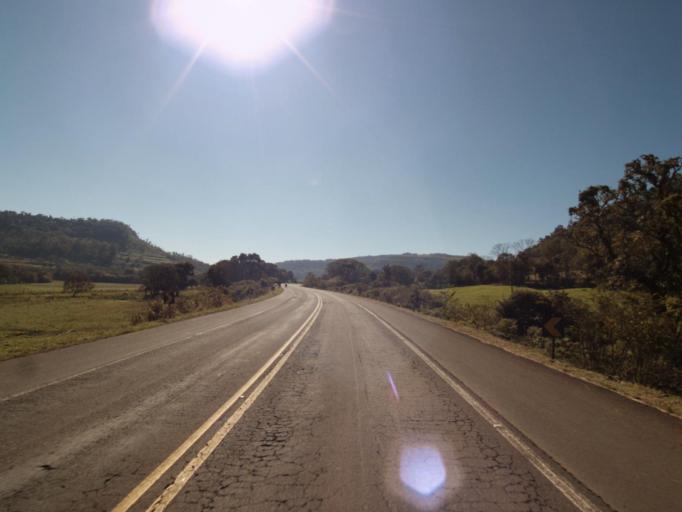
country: BR
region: Rio Grande do Sul
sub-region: Frederico Westphalen
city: Frederico Westphalen
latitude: -26.9836
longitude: -53.2222
